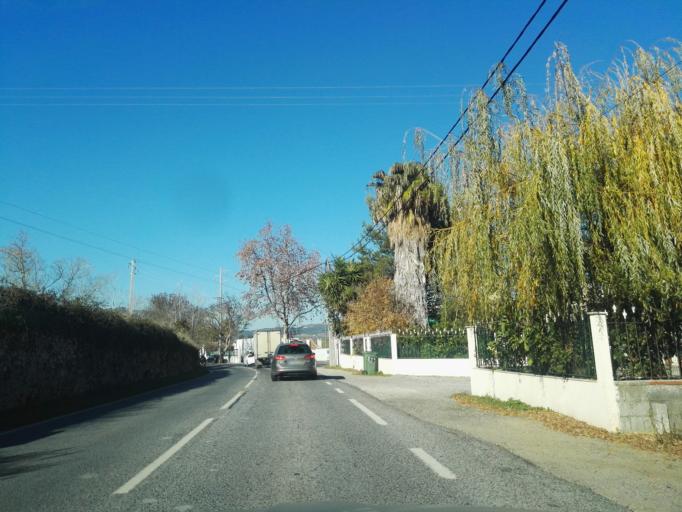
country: PT
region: Lisbon
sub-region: Arruda Dos Vinhos
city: Arruda dos Vinhos
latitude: 38.9776
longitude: -9.0687
